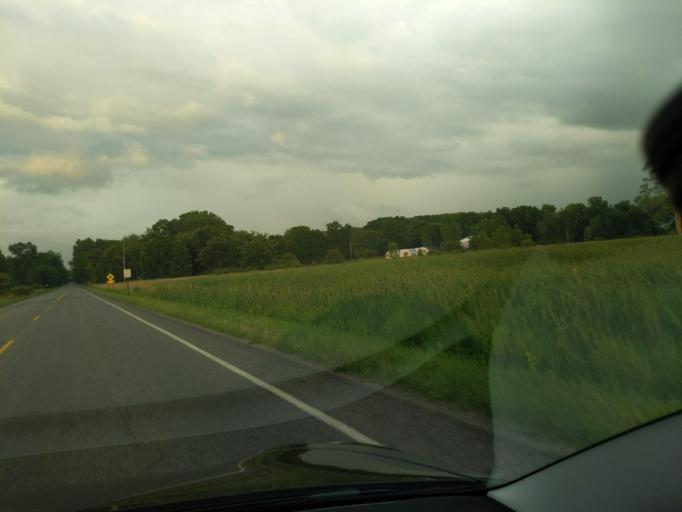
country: US
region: Michigan
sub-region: Ingham County
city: Mason
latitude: 42.5238
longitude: -84.3673
